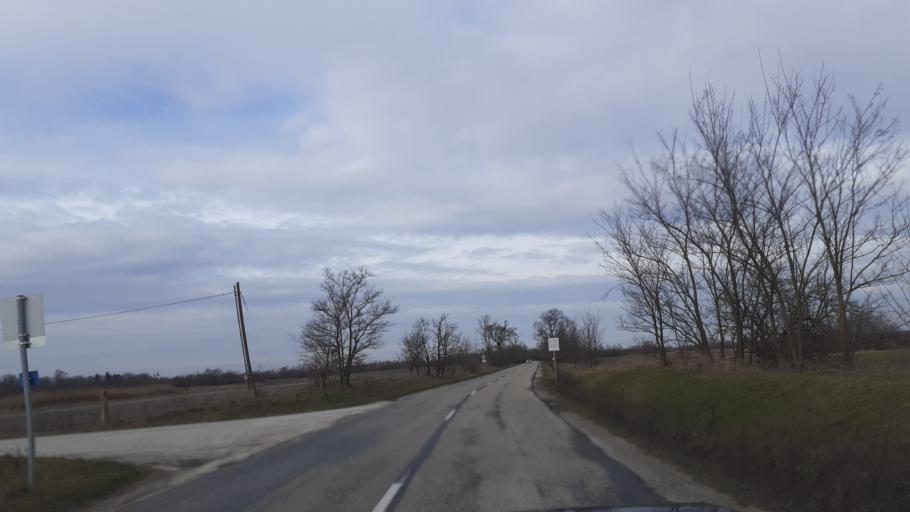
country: HU
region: Fejer
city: Soponya
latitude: 47.0685
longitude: 18.4167
